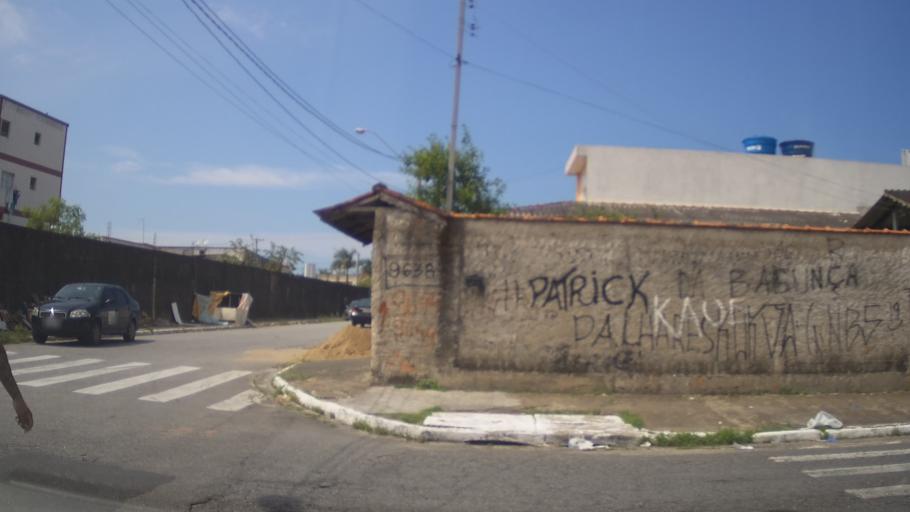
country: BR
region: Sao Paulo
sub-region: Praia Grande
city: Praia Grande
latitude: -24.0215
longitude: -46.4846
